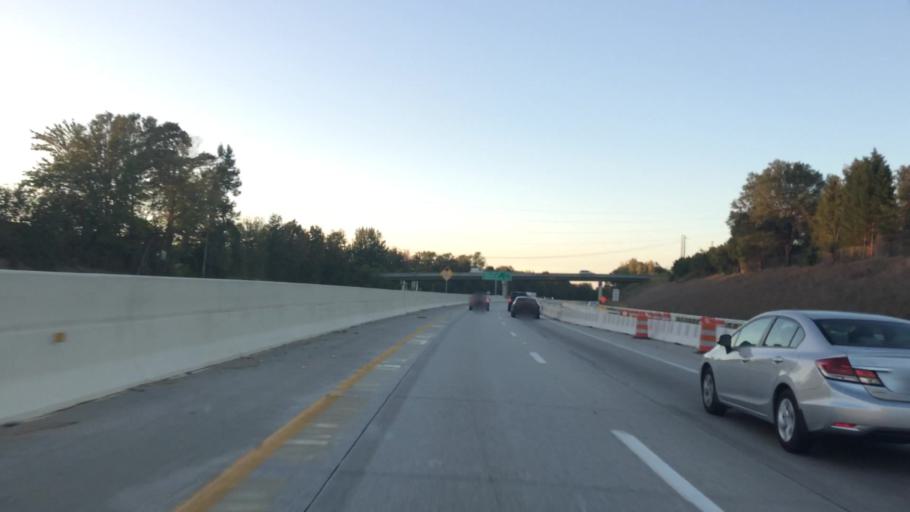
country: US
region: South Carolina
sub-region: Greenville County
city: Mauldin
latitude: 34.8130
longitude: -82.2882
